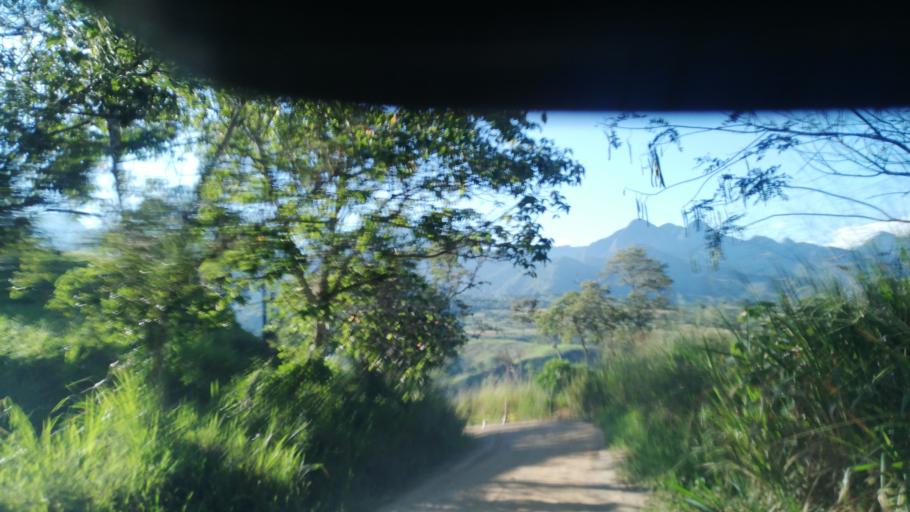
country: CO
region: Cundinamarca
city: Viani
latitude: 4.8358
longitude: -74.6199
